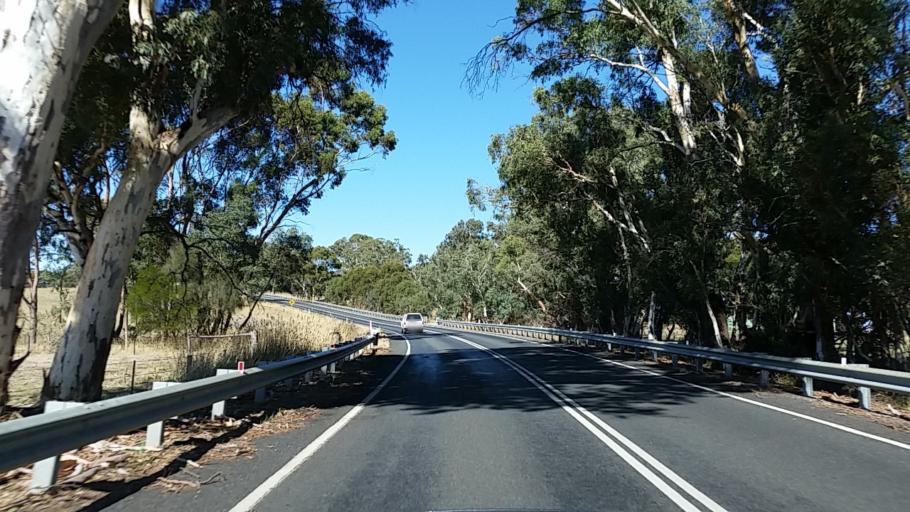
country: AU
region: South Australia
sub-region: Adelaide Hills
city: Birdwood
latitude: -34.7604
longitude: 139.0050
